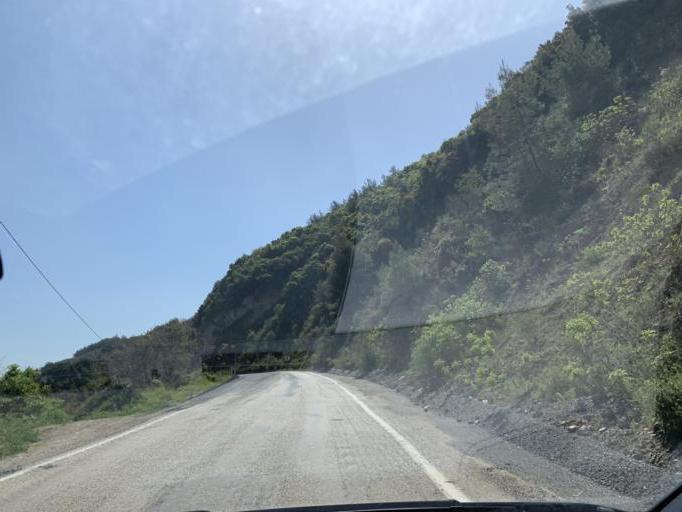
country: TR
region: Bursa
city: Niluefer
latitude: 40.3556
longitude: 28.9755
